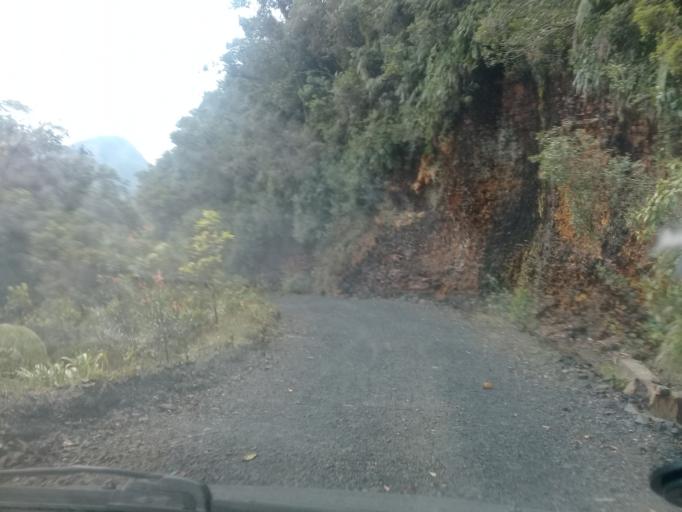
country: CO
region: Cundinamarca
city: Gachala
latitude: 4.7030
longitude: -73.4258
